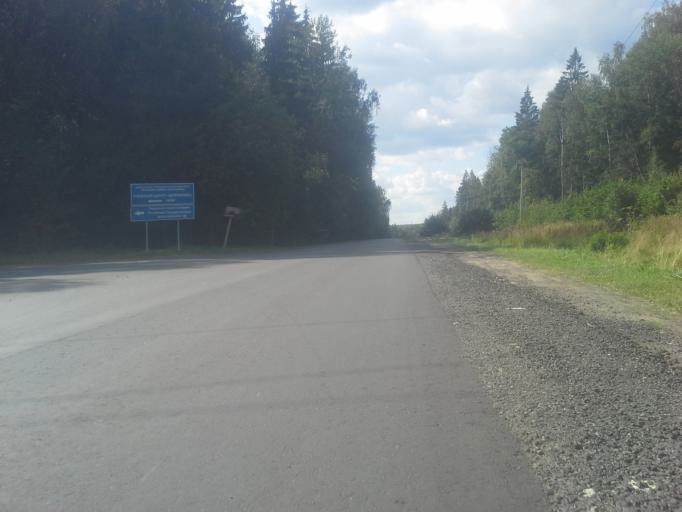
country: RU
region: Moskovskaya
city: Aprelevka
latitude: 55.3248
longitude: 37.1276
